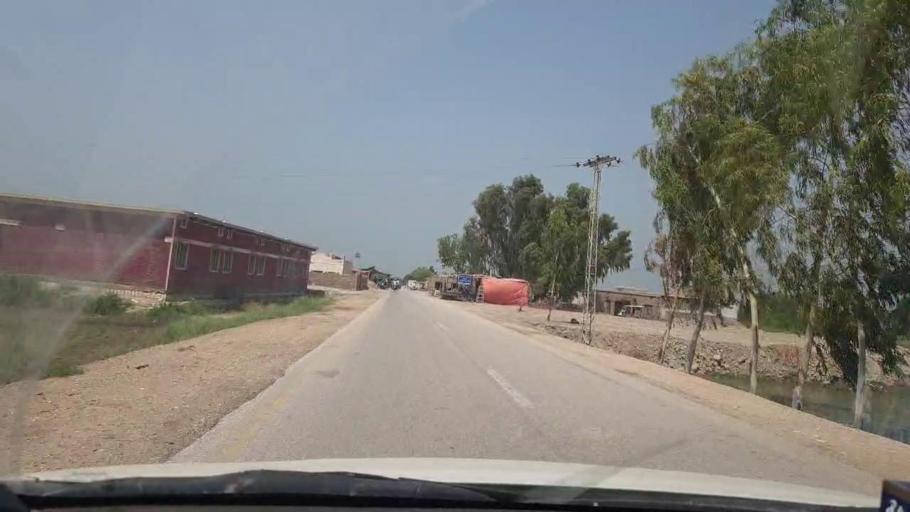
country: PK
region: Sindh
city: Rustam jo Goth
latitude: 27.9550
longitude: 68.7271
